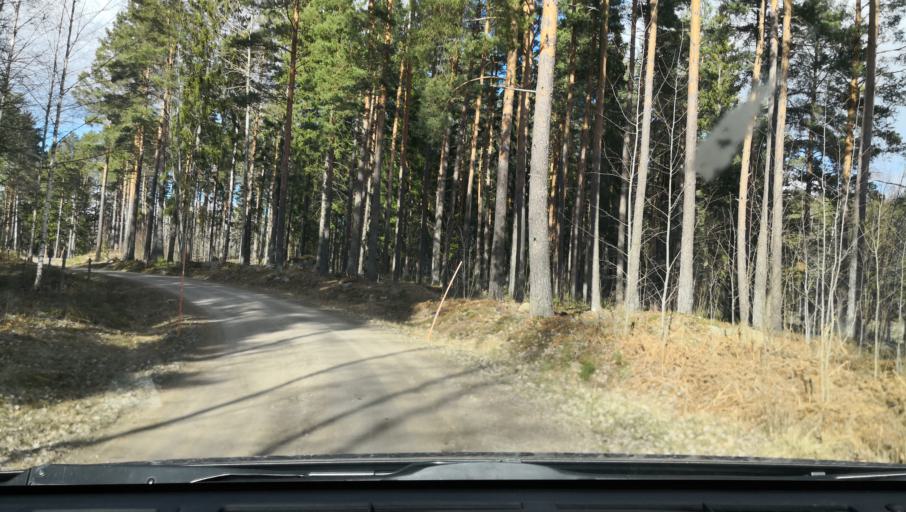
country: SE
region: OErebro
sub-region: Lindesbergs Kommun
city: Fellingsbro
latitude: 59.4281
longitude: 15.6868
